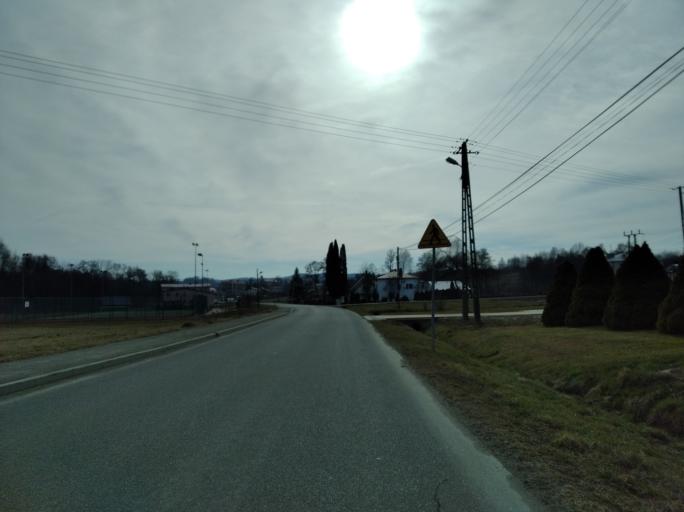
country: PL
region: Subcarpathian Voivodeship
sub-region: Powiat brzozowski
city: Orzechowka
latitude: 49.7336
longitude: 21.9436
